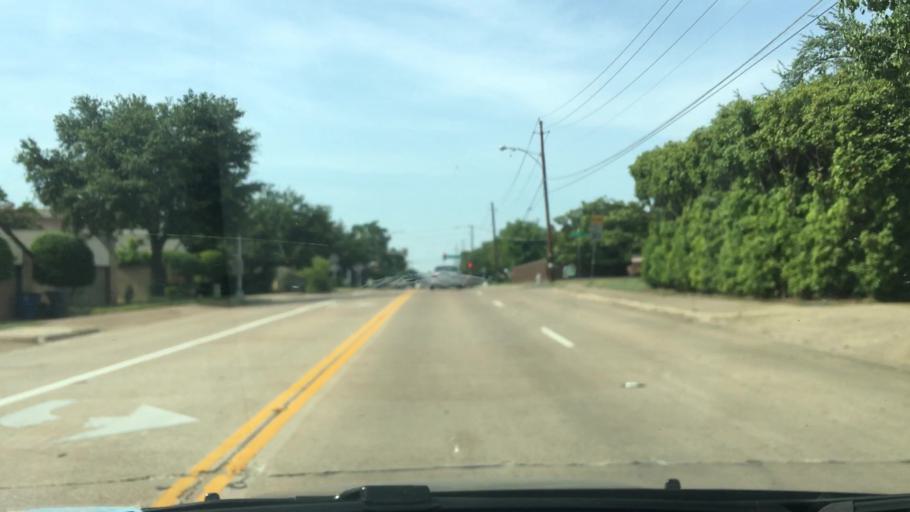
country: US
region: Texas
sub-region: Dallas County
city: Addison
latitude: 32.9212
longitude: -96.8113
